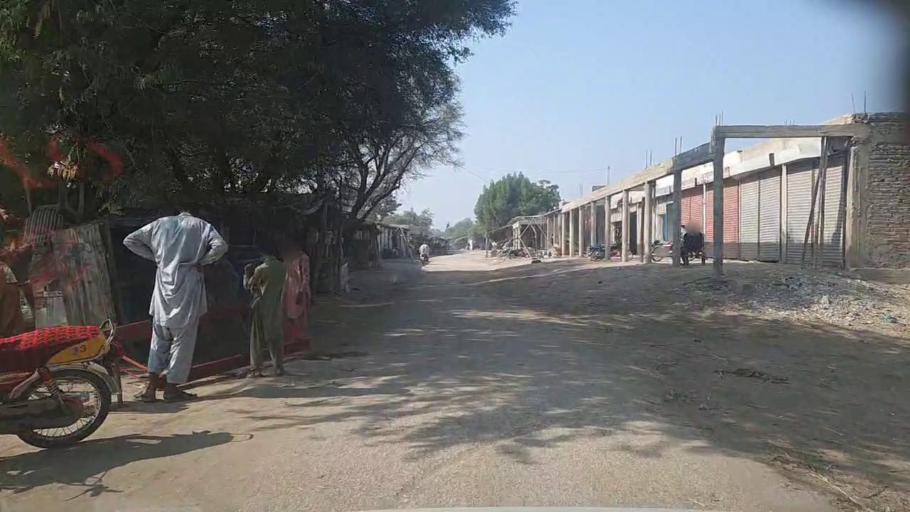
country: PK
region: Sindh
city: Karaundi
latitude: 26.9797
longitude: 68.4465
